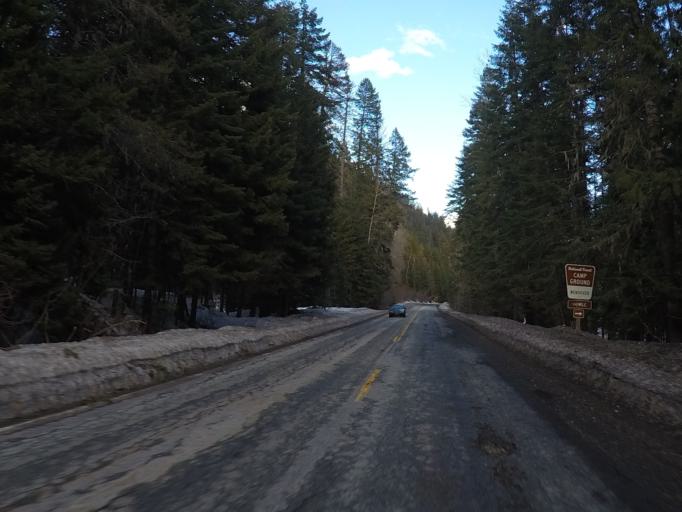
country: US
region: Montana
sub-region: Ravalli County
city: Hamilton
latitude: 46.5109
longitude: -114.7877
